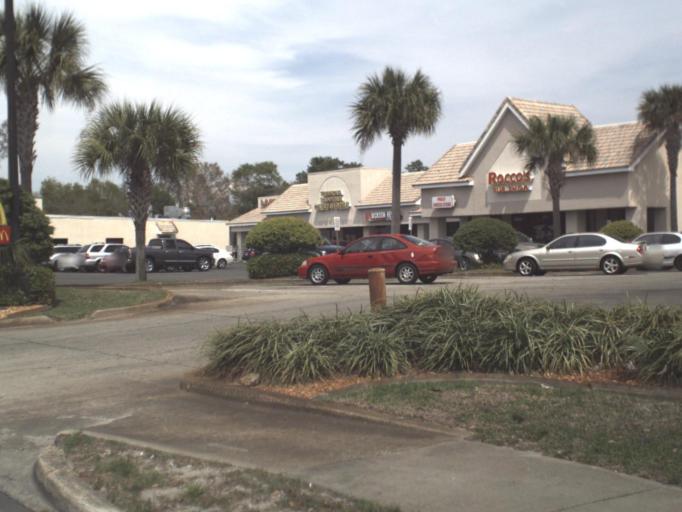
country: US
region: Florida
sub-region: Okaloosa County
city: Lake Lorraine
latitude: 30.4421
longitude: -86.5807
